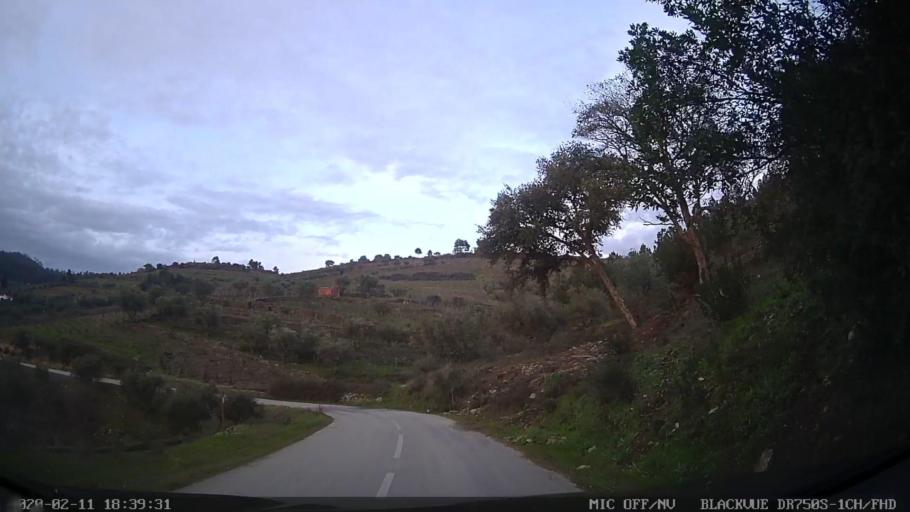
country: PT
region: Vila Real
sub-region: Sabrosa
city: Vilela
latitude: 41.1778
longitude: -7.5951
